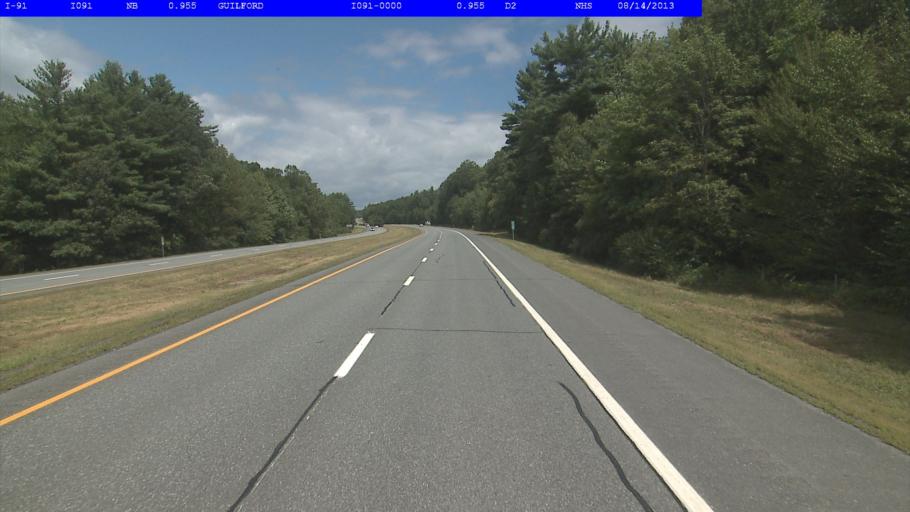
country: US
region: Massachusetts
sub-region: Franklin County
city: Bernardston
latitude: 42.7437
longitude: -72.5666
